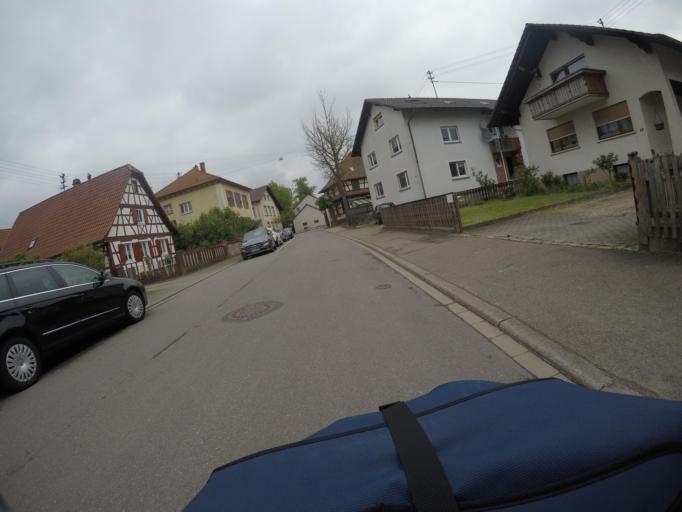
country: DE
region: Baden-Wuerttemberg
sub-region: Karlsruhe Region
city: Iffezheim
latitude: 48.8458
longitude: 8.1381
